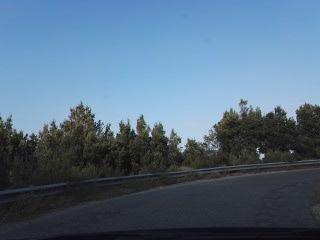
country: IT
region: Calabria
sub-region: Provincia di Vibo-Valentia
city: Nardodipace
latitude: 38.4345
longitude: 16.3438
